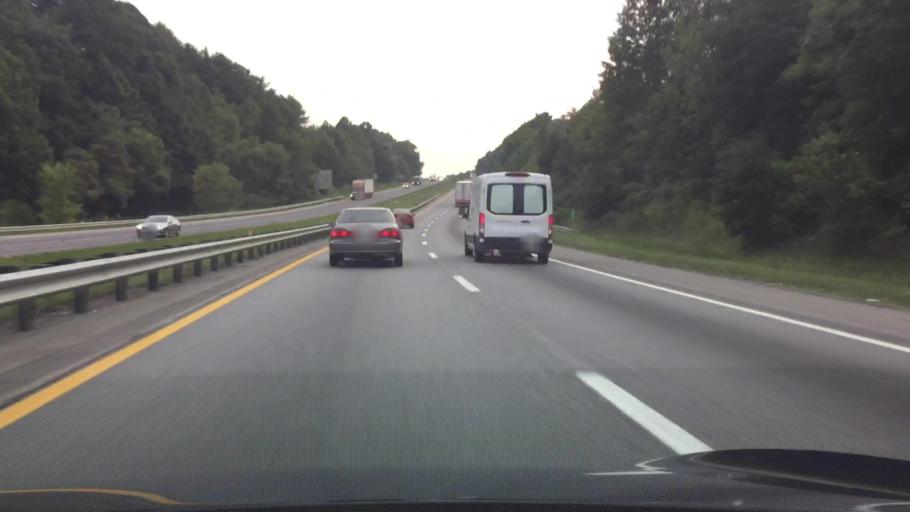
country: US
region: Virginia
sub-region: Pulaski County
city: Pulaski
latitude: 37.0145
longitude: -80.7420
